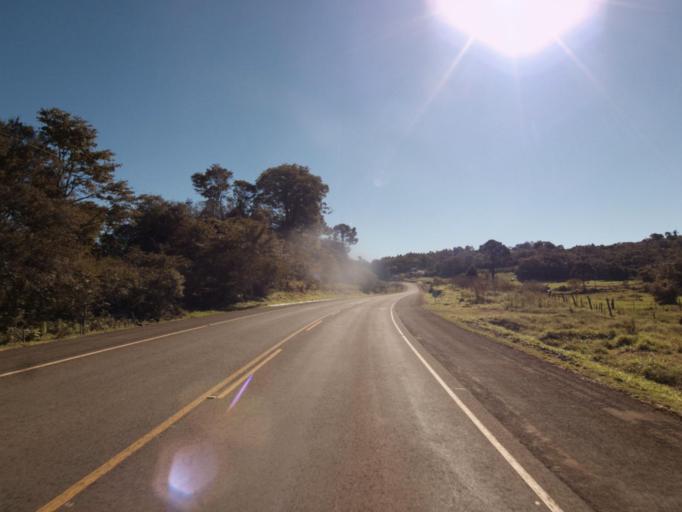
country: AR
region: Misiones
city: Bernardo de Irigoyen
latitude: -26.6743
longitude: -53.5679
